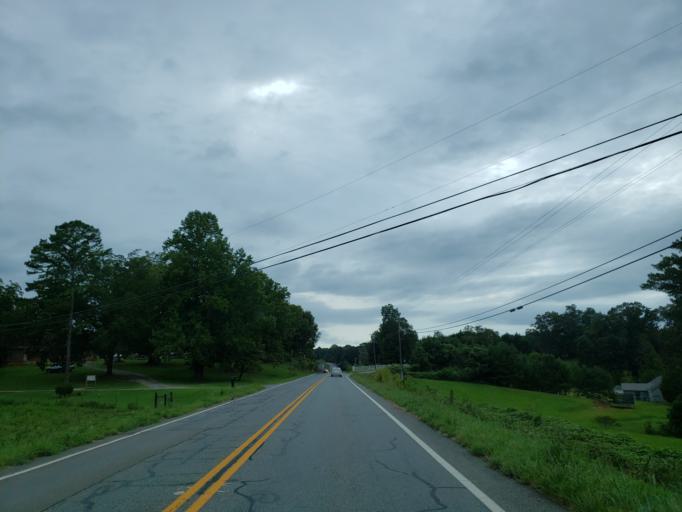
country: US
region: Georgia
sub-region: Gilmer County
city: Ellijay
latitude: 34.6420
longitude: -84.5433
